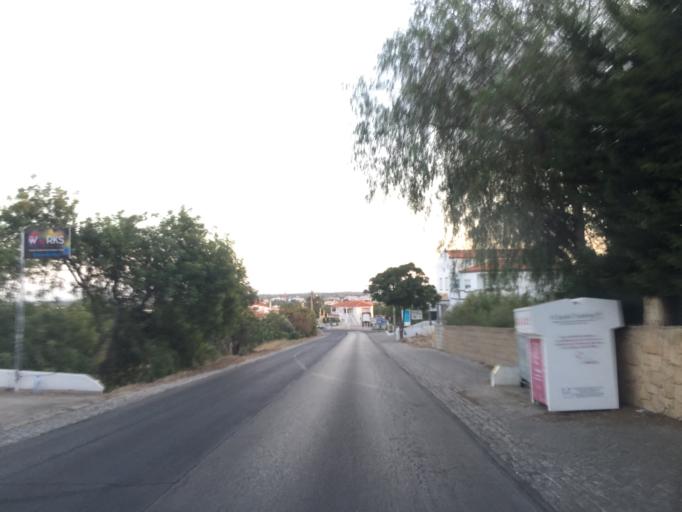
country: PT
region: Faro
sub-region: Loule
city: Almancil
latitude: 37.0983
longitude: -8.0239
